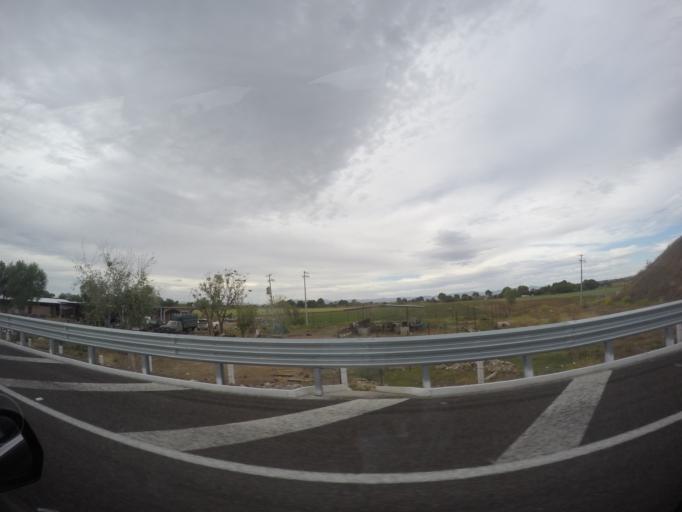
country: MX
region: Guanajuato
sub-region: Irapuato
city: Serrano
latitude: 20.7769
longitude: -101.4057
